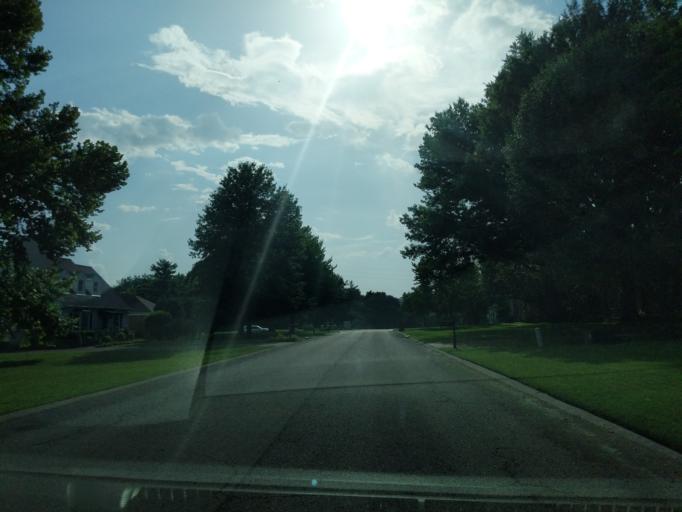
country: US
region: Tennessee
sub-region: Davidson County
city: Forest Hills
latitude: 36.0288
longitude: -86.9508
